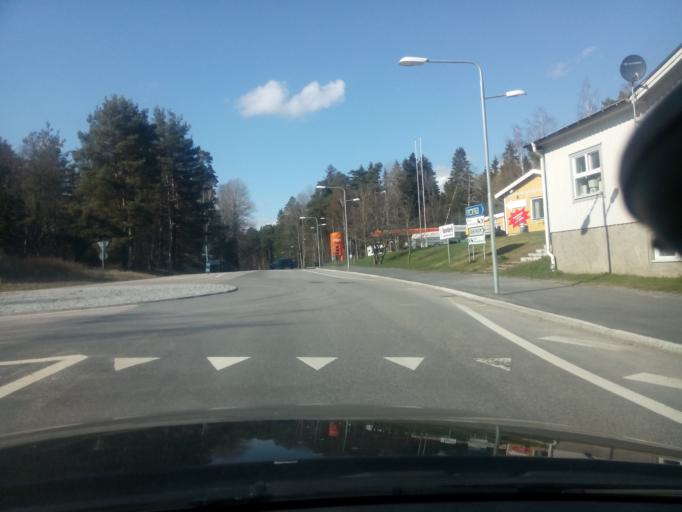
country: SE
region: Soedermanland
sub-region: Flens Kommun
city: Malmkoping
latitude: 59.1403
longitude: 16.7185
